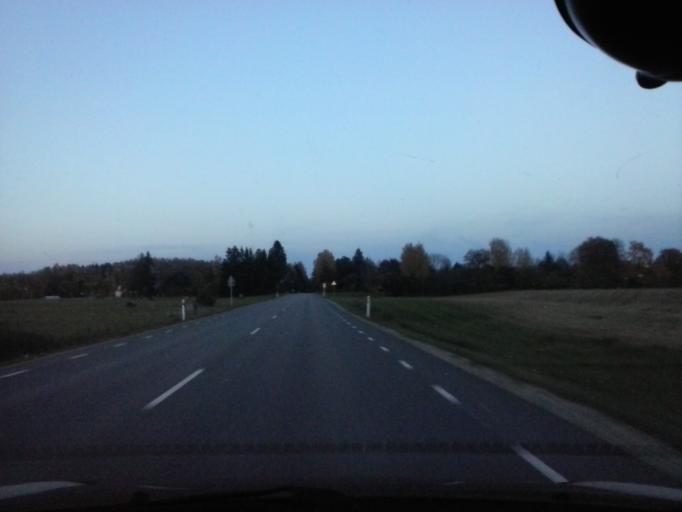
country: EE
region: Raplamaa
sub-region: Rapla vald
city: Rapla
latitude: 58.9790
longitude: 24.7320
